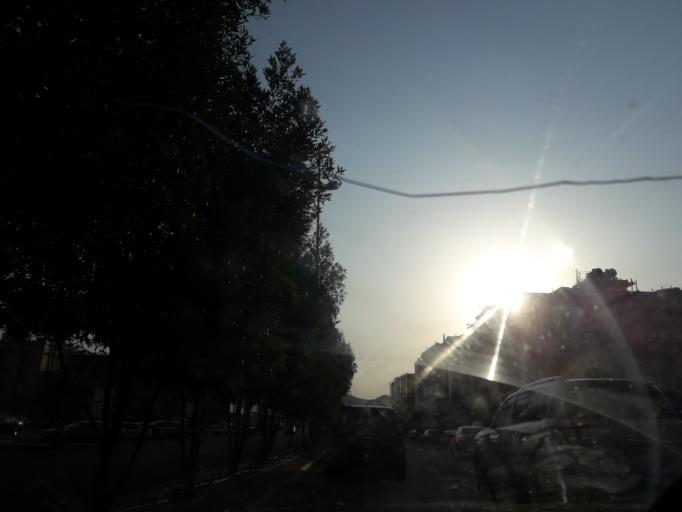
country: SA
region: Makkah
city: Ta'if
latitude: 21.3205
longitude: 40.4326
